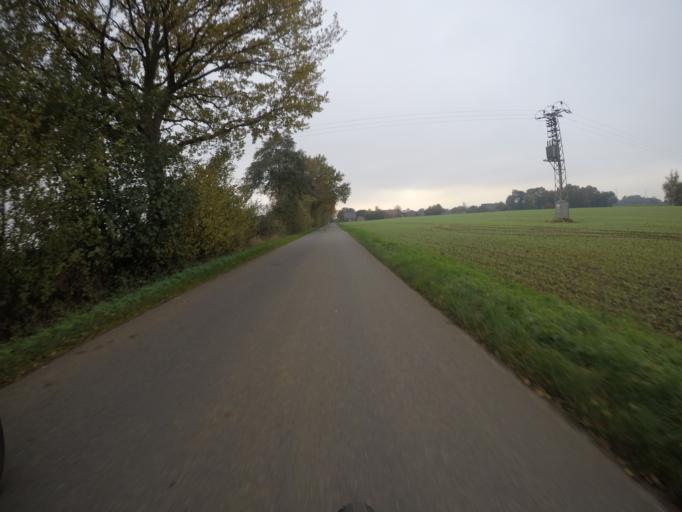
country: DE
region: North Rhine-Westphalia
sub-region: Regierungsbezirk Munster
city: Isselburg
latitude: 51.8238
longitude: 6.5391
